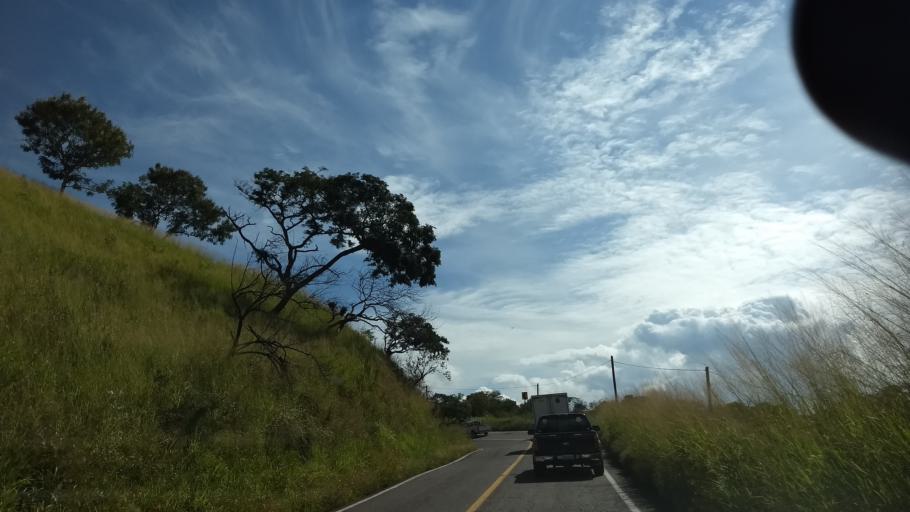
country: MX
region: Jalisco
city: Tuxpan
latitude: 19.5233
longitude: -103.4228
